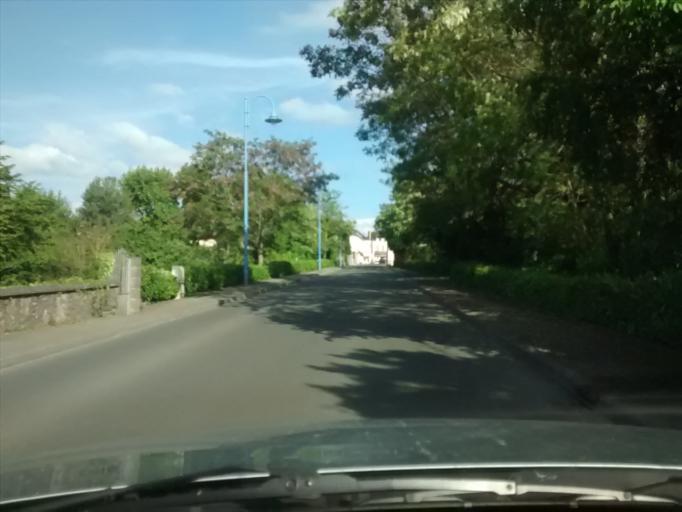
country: FR
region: Pays de la Loire
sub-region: Departement de la Mayenne
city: Entrammes
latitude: 47.9226
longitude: -0.6790
